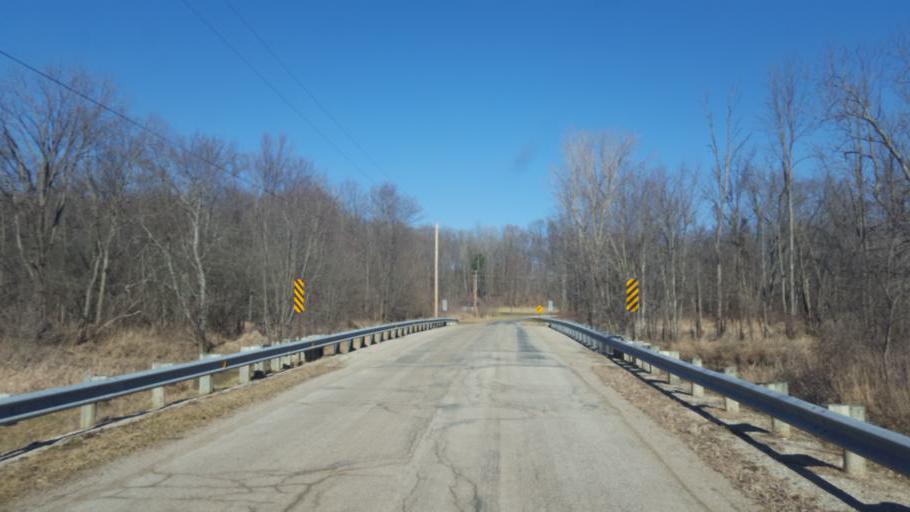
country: US
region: Ohio
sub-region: Richland County
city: Lincoln Heights
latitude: 40.8717
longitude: -82.4604
